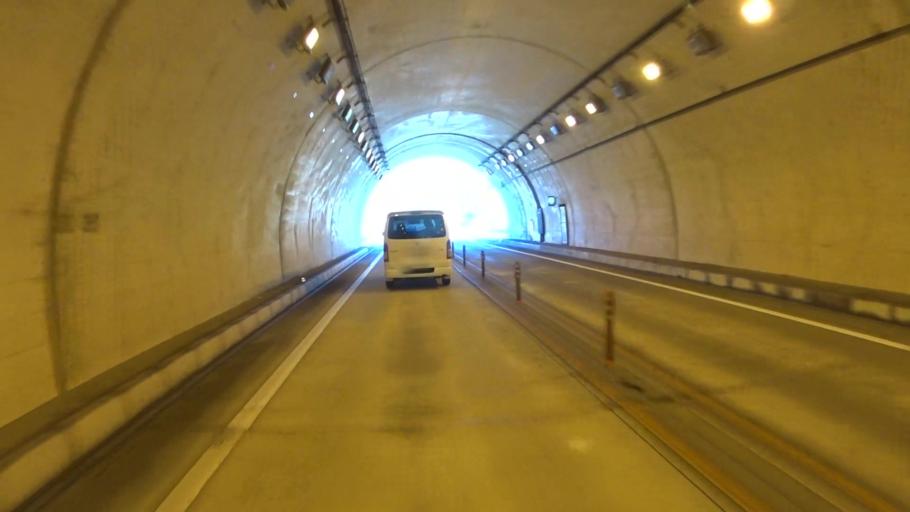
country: JP
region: Kyoto
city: Miyazu
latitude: 35.4600
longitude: 135.1745
